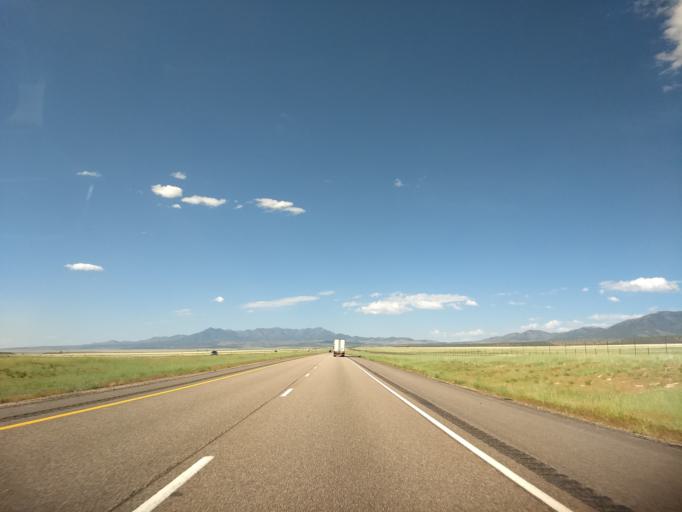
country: US
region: Utah
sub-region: Millard County
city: Fillmore
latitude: 39.0284
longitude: -112.3001
